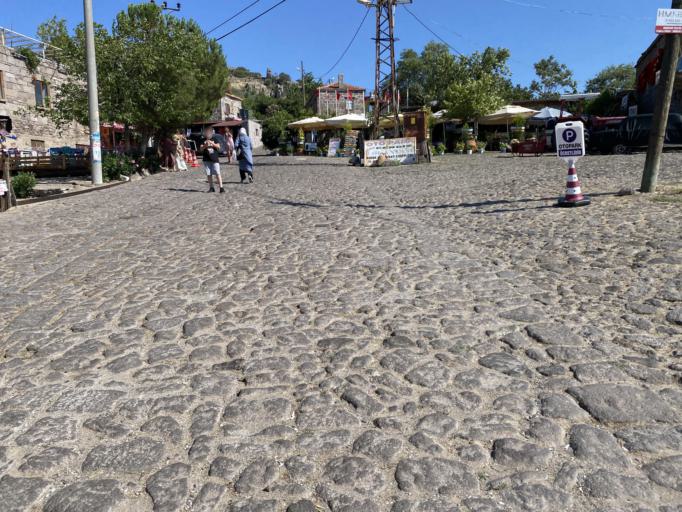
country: TR
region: Canakkale
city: Behram
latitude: 39.4929
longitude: 26.3334
